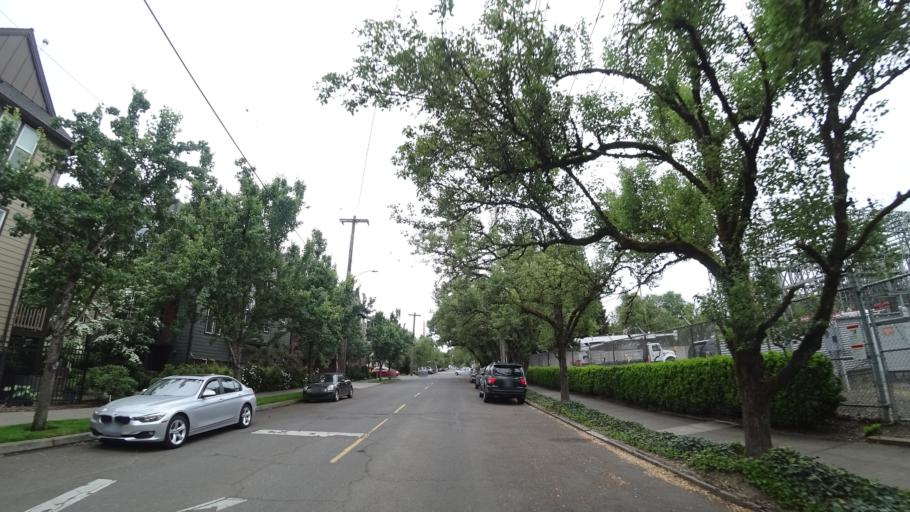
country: US
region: Oregon
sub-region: Clackamas County
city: Milwaukie
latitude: 45.4587
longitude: -122.6530
